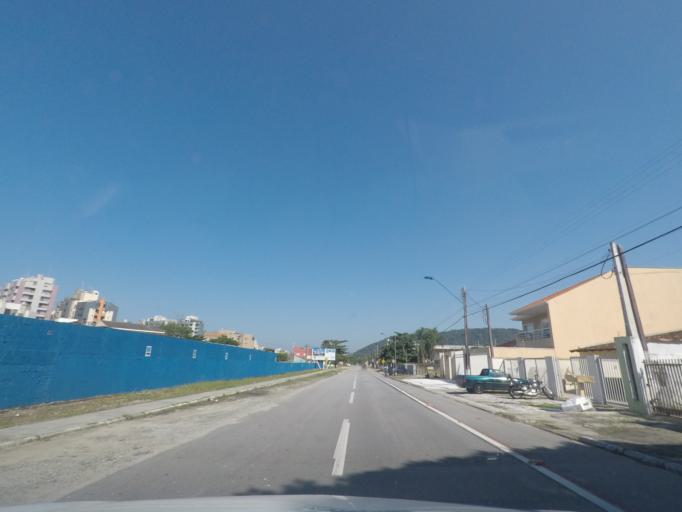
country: BR
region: Parana
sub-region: Guaratuba
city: Guaratuba
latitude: -25.8297
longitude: -48.5388
